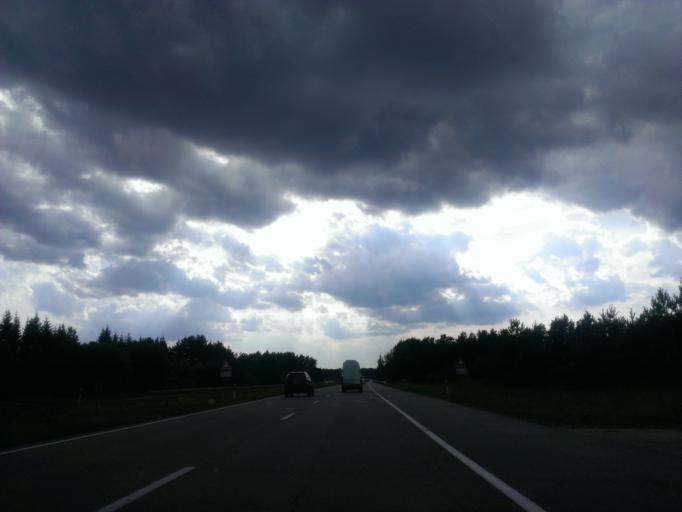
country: LV
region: Incukalns
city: Incukalns
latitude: 57.1294
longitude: 24.7250
